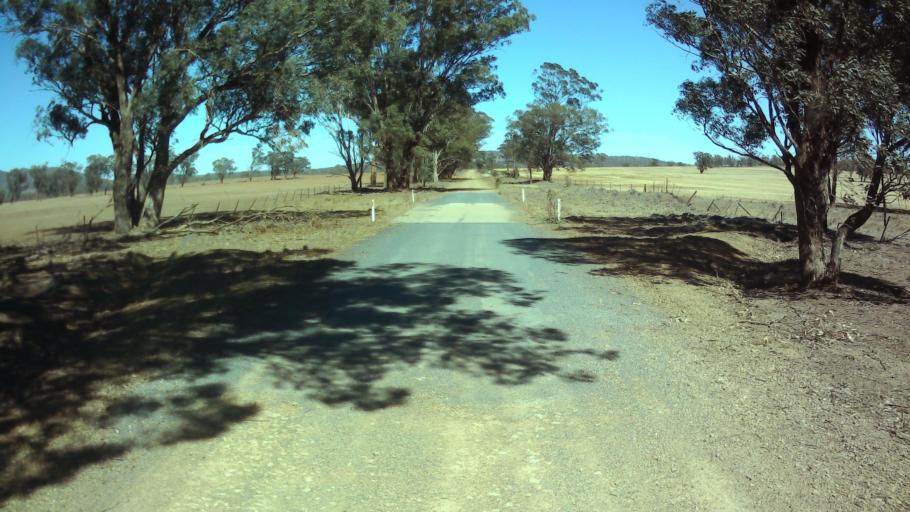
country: AU
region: New South Wales
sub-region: Weddin
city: Grenfell
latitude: -33.7077
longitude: 147.9982
